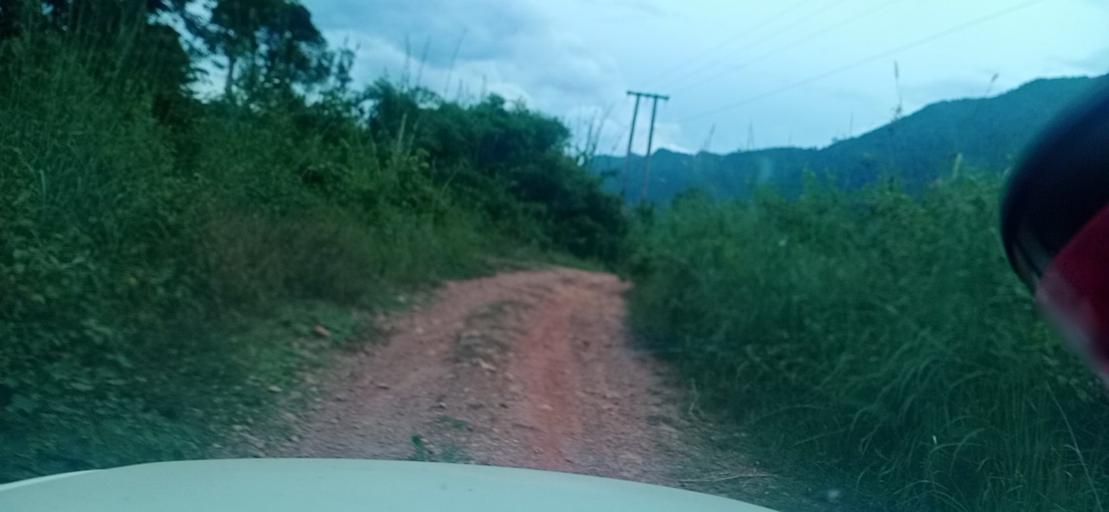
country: TH
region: Changwat Bueng Kan
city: Pak Khat
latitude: 18.5624
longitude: 103.2874
